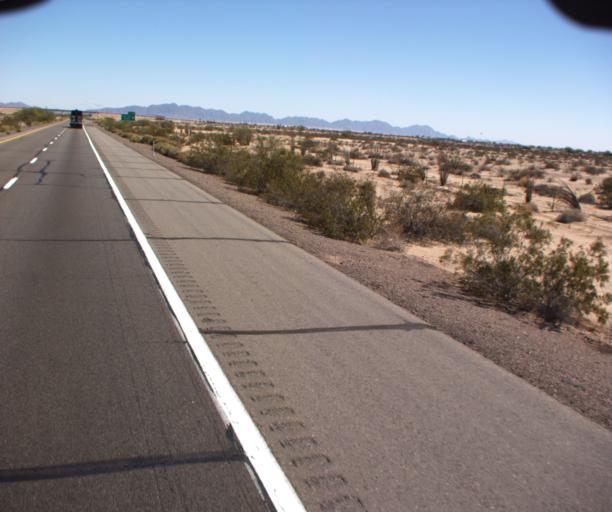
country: US
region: Arizona
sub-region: Yuma County
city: Wellton
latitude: 32.6921
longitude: -113.9614
